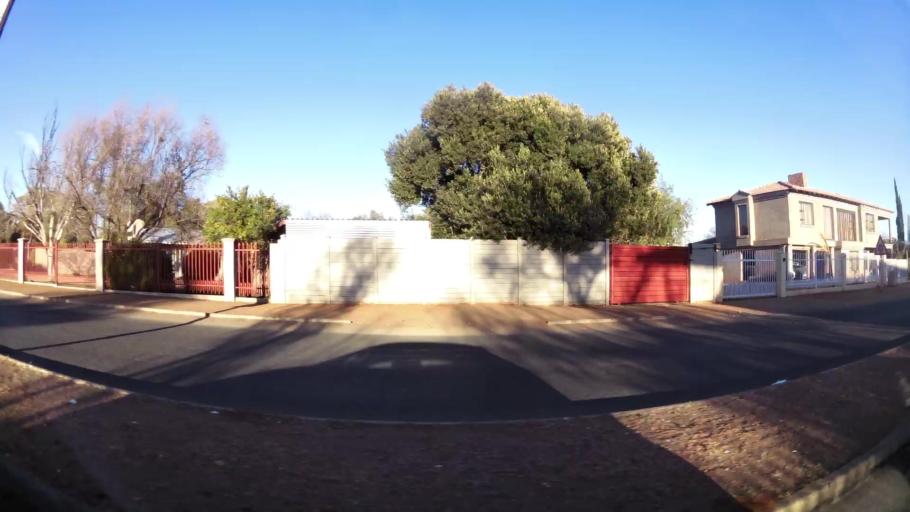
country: ZA
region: Northern Cape
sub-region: Frances Baard District Municipality
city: Kimberley
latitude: -28.7529
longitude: 24.7454
